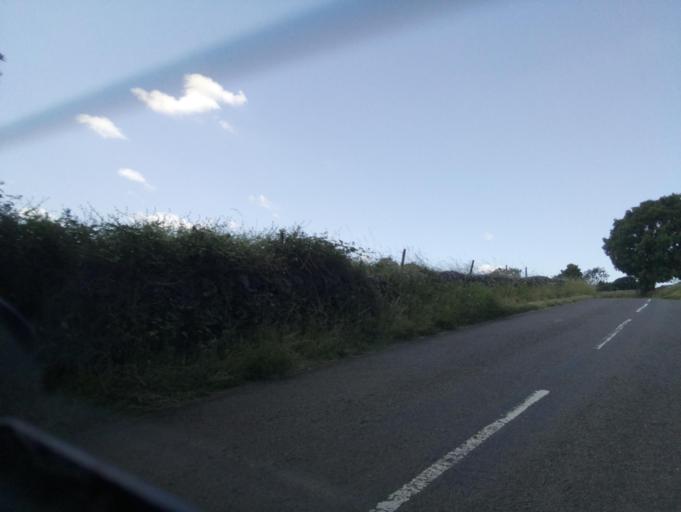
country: GB
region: England
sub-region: Derbyshire
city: Tideswell
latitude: 53.2599
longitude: -1.8040
